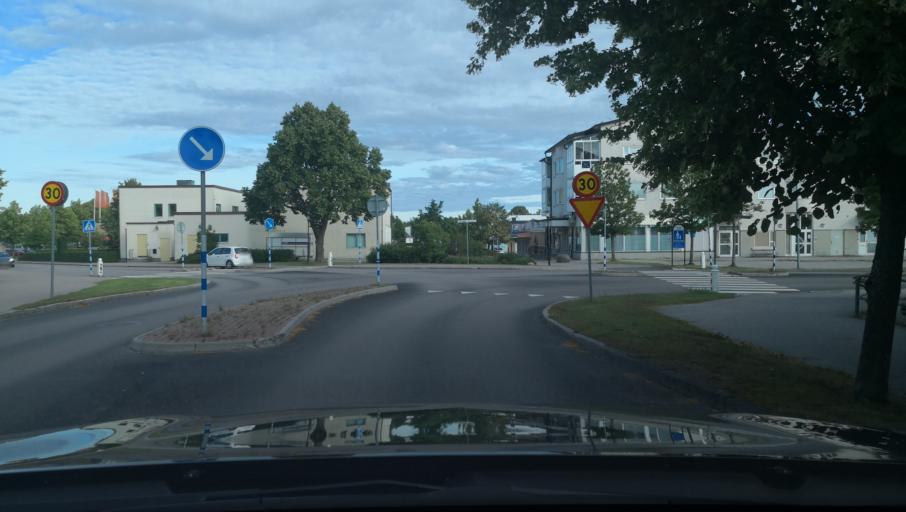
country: SE
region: Vaestmanland
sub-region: Hallstahammars Kommun
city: Hallstahammar
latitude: 59.6152
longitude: 16.2260
